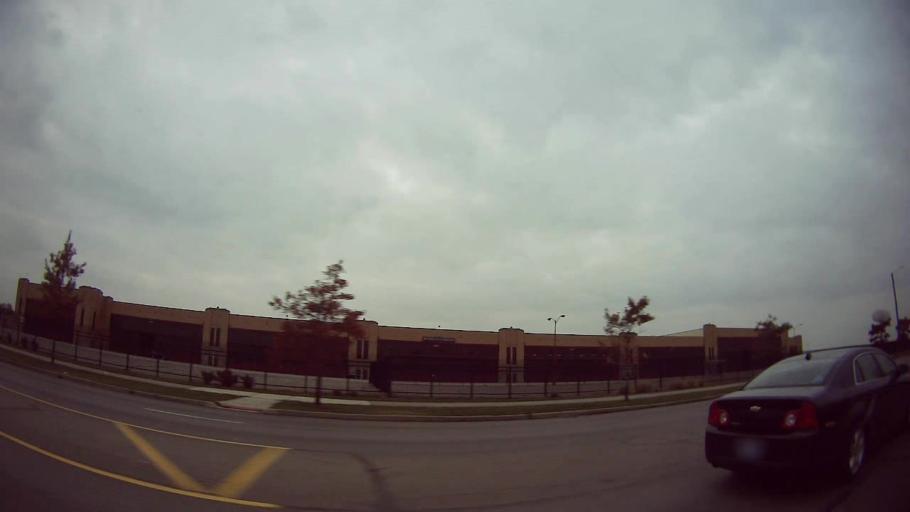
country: US
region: Michigan
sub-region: Wayne County
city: Hamtramck
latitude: 42.4059
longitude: -82.9986
